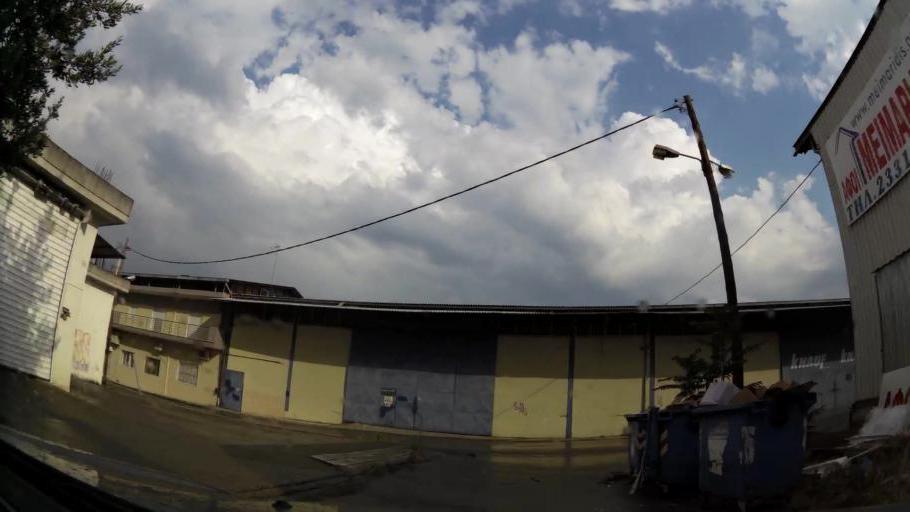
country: GR
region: Central Macedonia
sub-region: Nomos Imathias
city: Veroia
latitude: 40.5403
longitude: 22.2013
